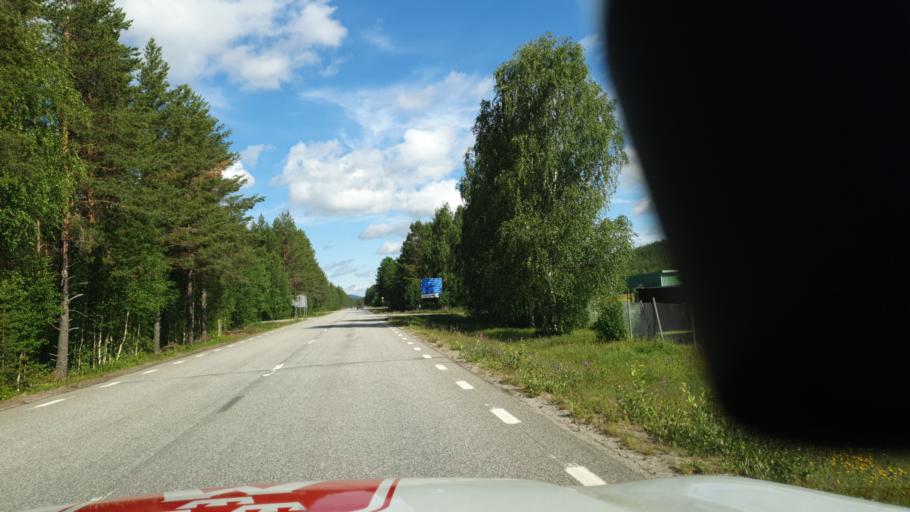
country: SE
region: Vaesterbotten
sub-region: Norsjo Kommun
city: Norsjoe
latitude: 64.5784
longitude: 19.3043
